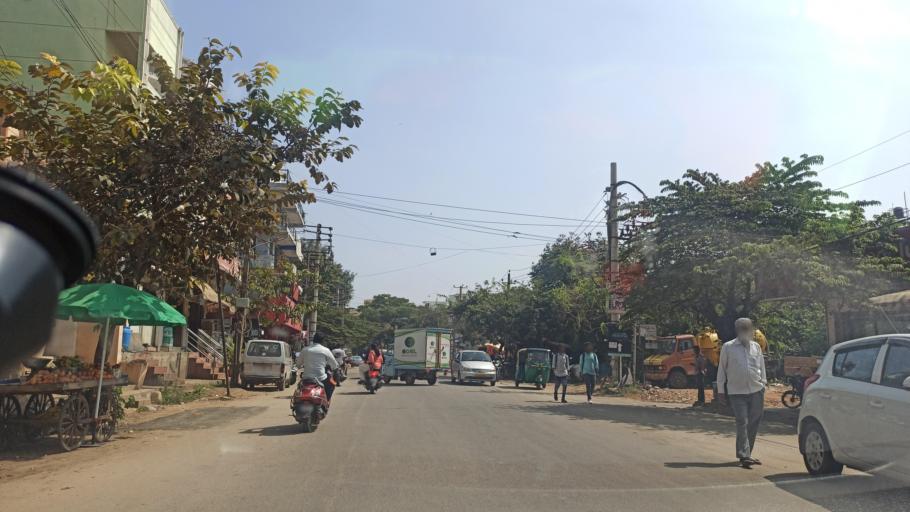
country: IN
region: Karnataka
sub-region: Bangalore Urban
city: Yelahanka
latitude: 13.0662
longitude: 77.5978
